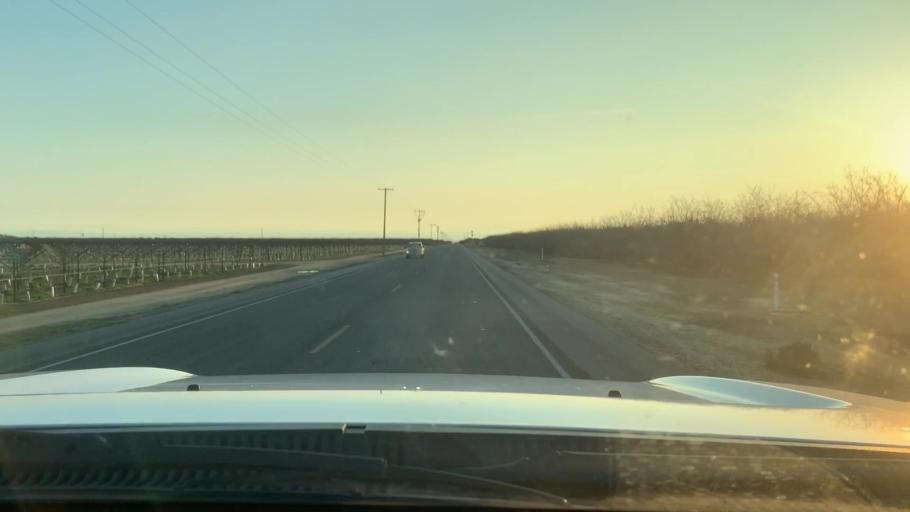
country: US
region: California
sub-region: Kern County
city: Buttonwillow
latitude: 35.5005
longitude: -119.4264
